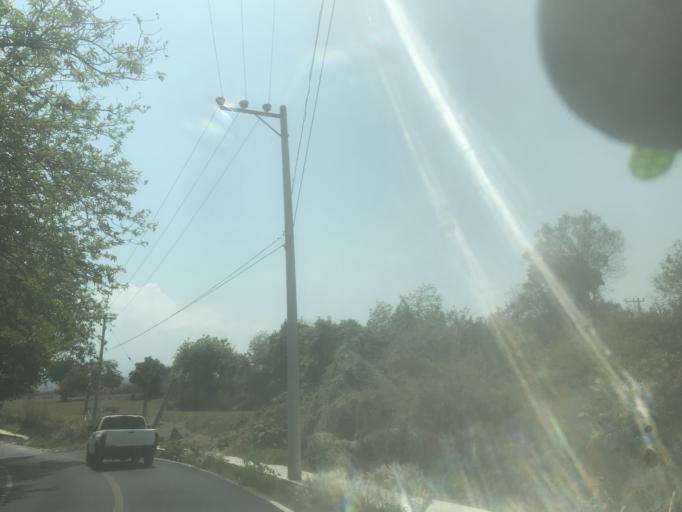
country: MX
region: Morelos
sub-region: Yecapixtla
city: Achichipico
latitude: 18.9631
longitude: -98.8244
